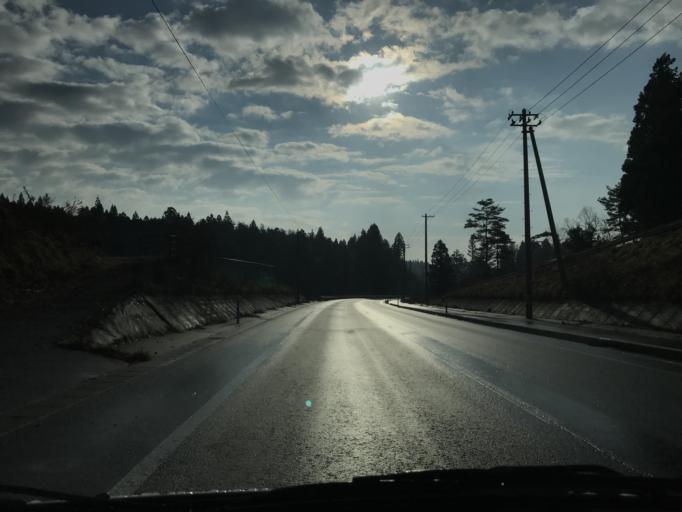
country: JP
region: Iwate
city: Ichinoseki
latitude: 38.8656
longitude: 141.1620
